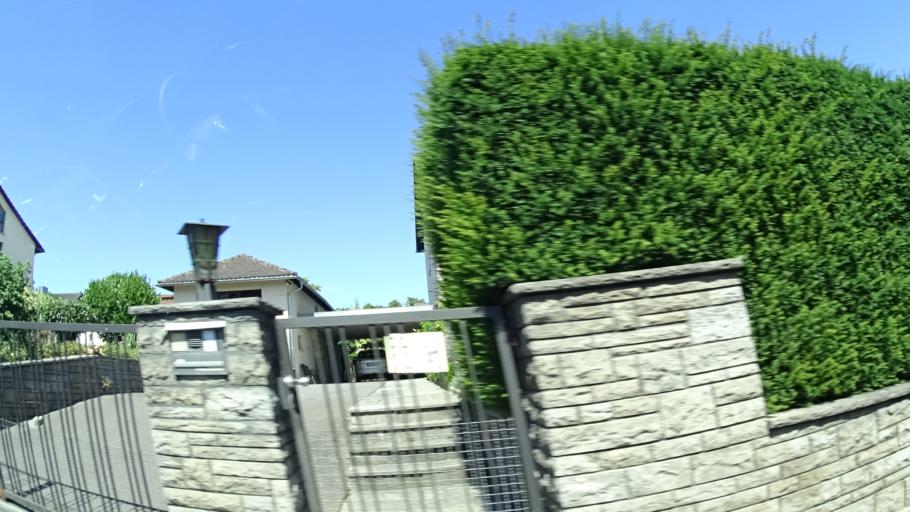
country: DE
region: Bavaria
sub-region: Regierungsbezirk Unterfranken
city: Rimpar
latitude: 49.8585
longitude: 9.9485
